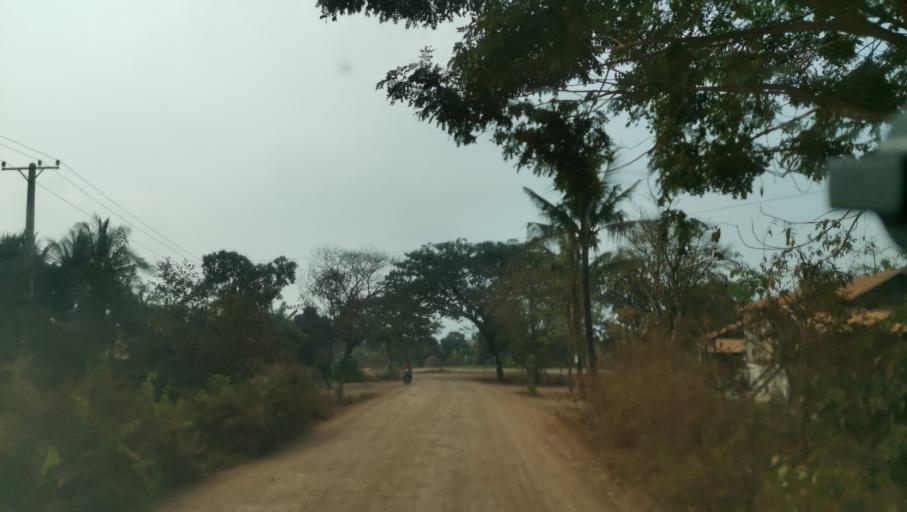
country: KH
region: Battambang
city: Battambang
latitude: 13.0575
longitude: 103.1691
